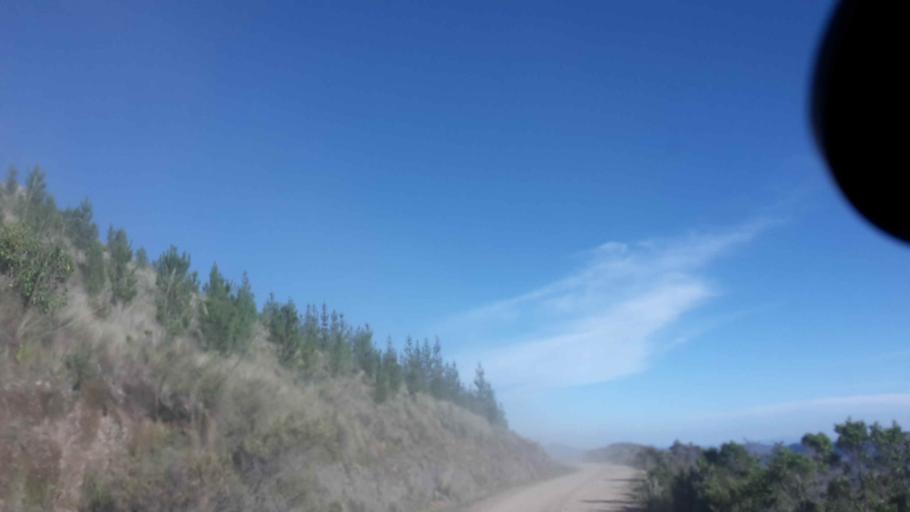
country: BO
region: Cochabamba
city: Arani
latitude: -17.7225
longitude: -65.6434
